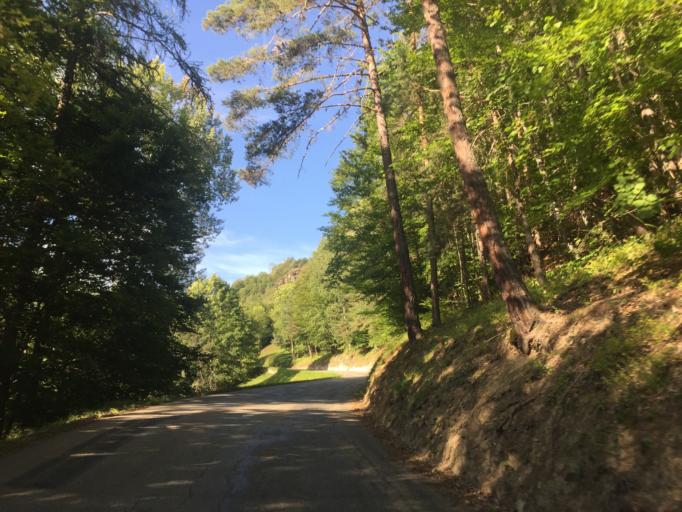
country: FR
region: Rhone-Alpes
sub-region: Departement de la Savoie
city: Moutiers
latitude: 45.5065
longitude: 6.5868
